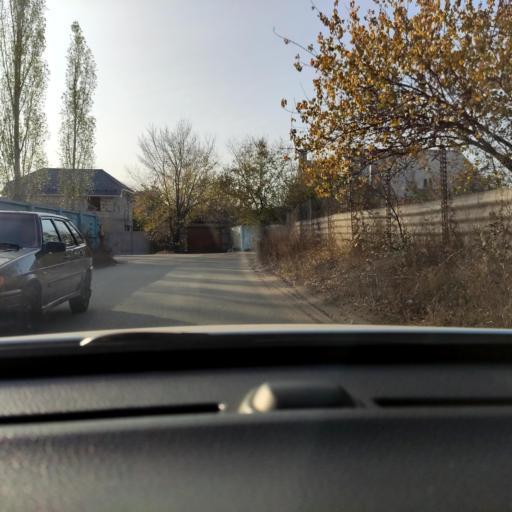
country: RU
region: Voronezj
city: Voronezh
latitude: 51.6683
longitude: 39.2874
